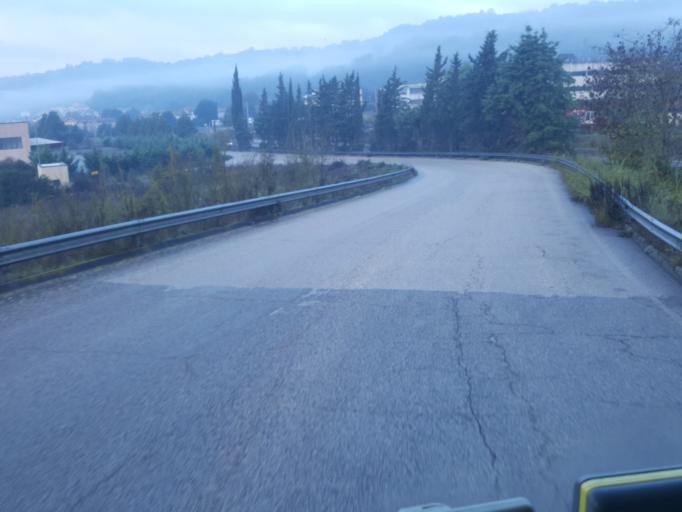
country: IT
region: Umbria
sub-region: Provincia di Terni
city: Fornole
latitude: 42.4825
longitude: 12.4486
